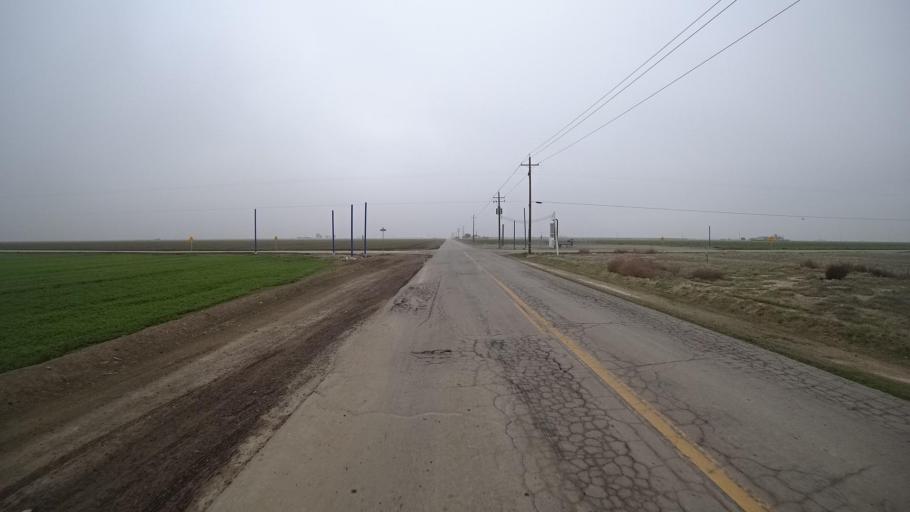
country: US
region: California
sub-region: Kern County
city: Wasco
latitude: 35.6742
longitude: -119.5088
